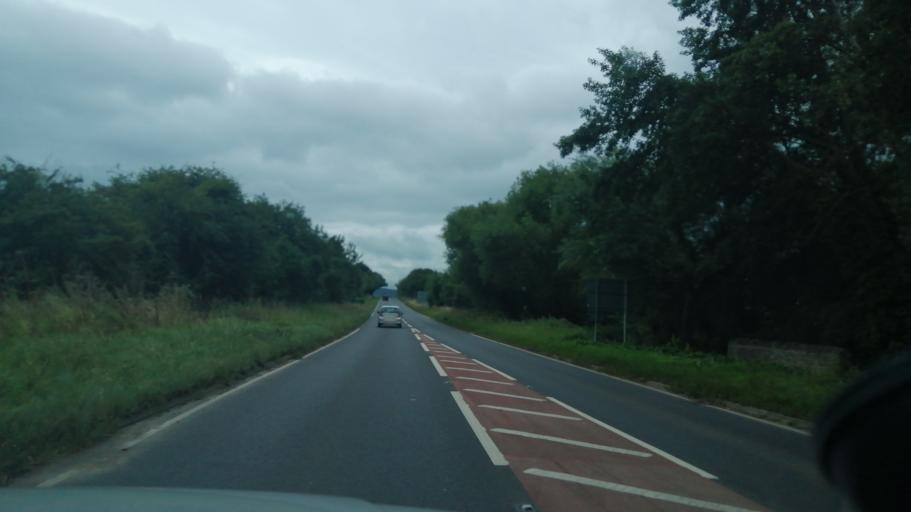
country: GB
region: England
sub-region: Herefordshire
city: Thruxton
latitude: 51.9984
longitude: -2.7924
